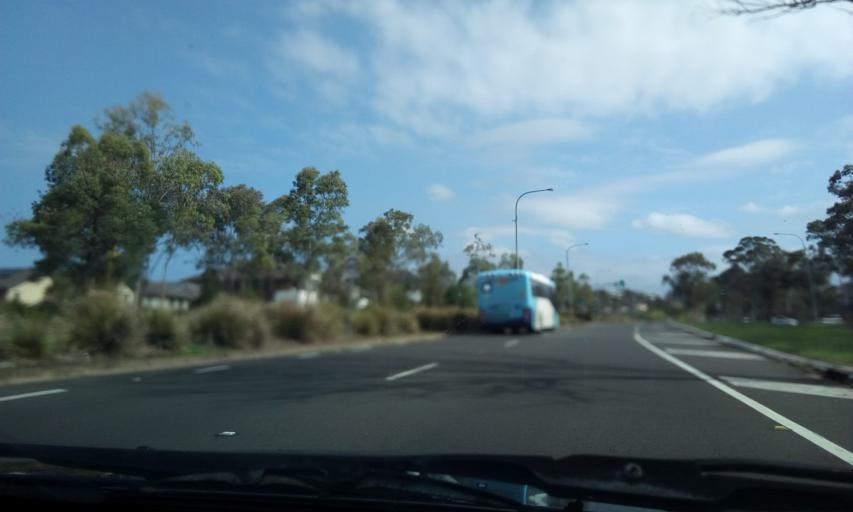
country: AU
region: New South Wales
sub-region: Campbelltown Municipality
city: Campbelltown
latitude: -34.0741
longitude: 150.8006
